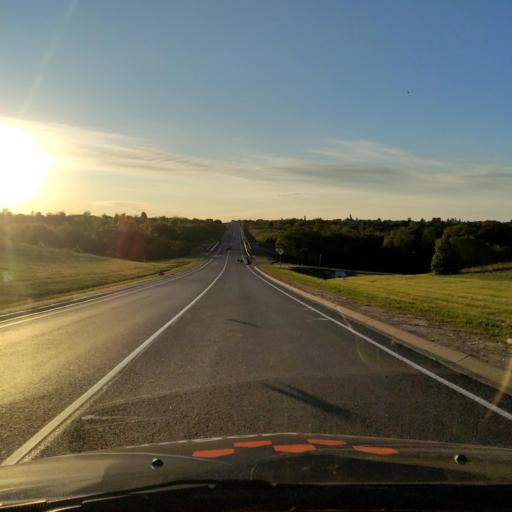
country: RU
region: Orjol
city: Livny
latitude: 52.4494
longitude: 37.6112
